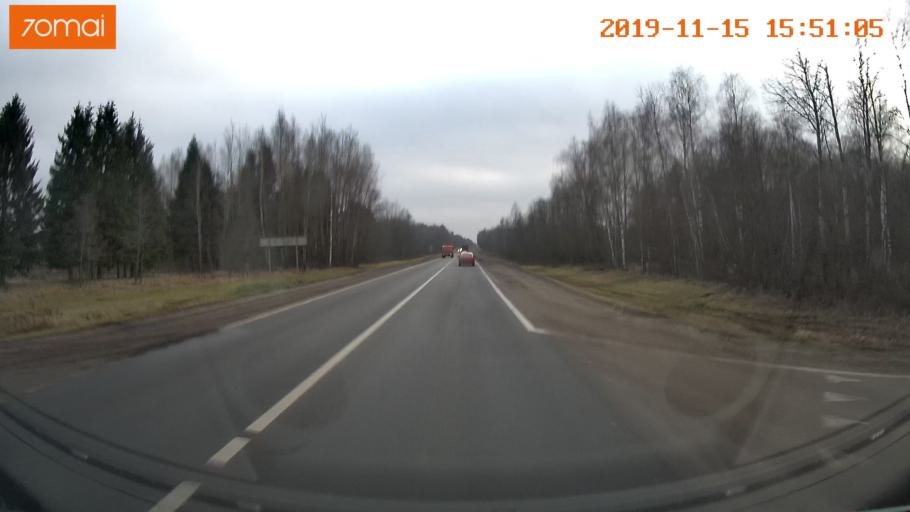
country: RU
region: Jaroslavl
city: Yaroslavl
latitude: 57.8987
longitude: 40.0102
